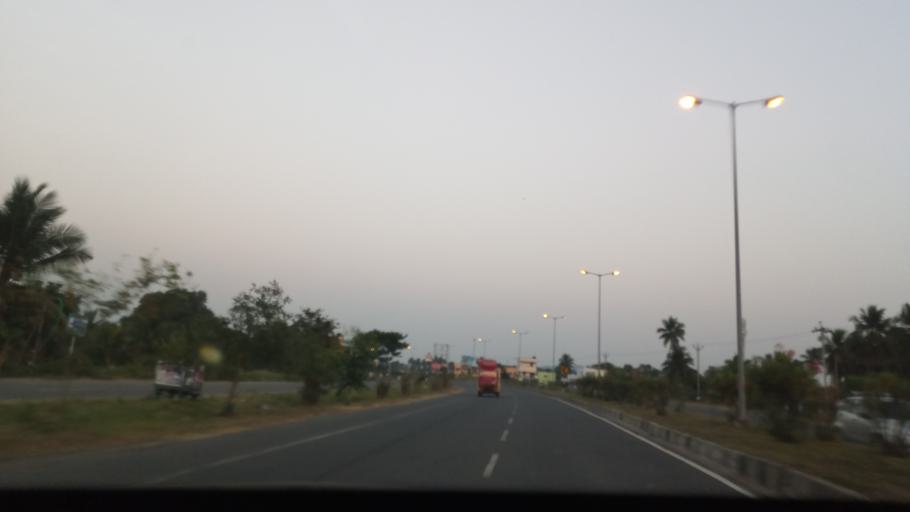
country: IN
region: Tamil Nadu
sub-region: Salem
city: Belur
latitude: 11.6522
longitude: 78.3490
